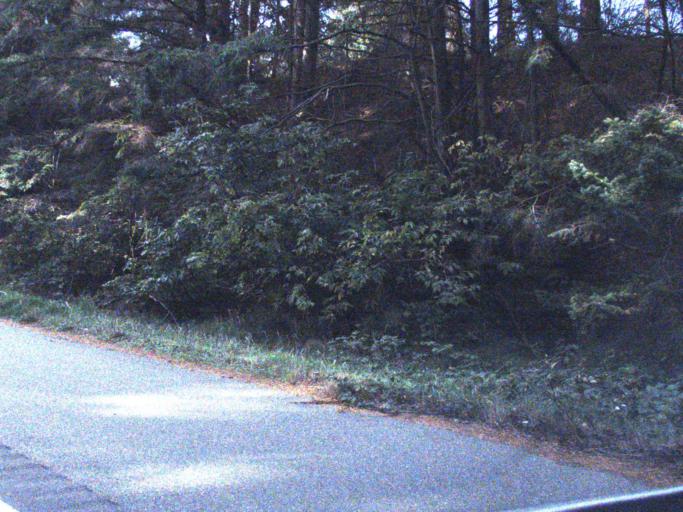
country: US
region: Washington
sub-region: Island County
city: Ault Field
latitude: 48.3579
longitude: -122.6163
